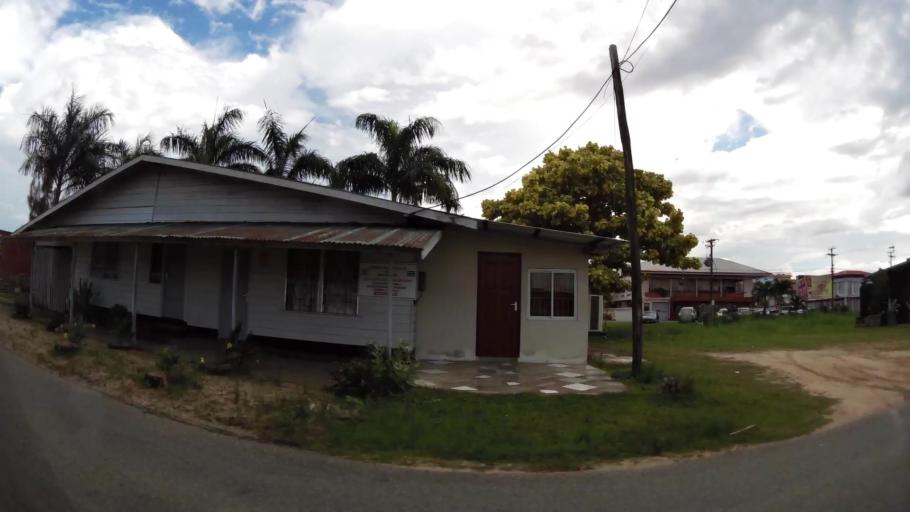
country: SR
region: Paramaribo
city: Paramaribo
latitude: 5.8404
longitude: -55.1391
